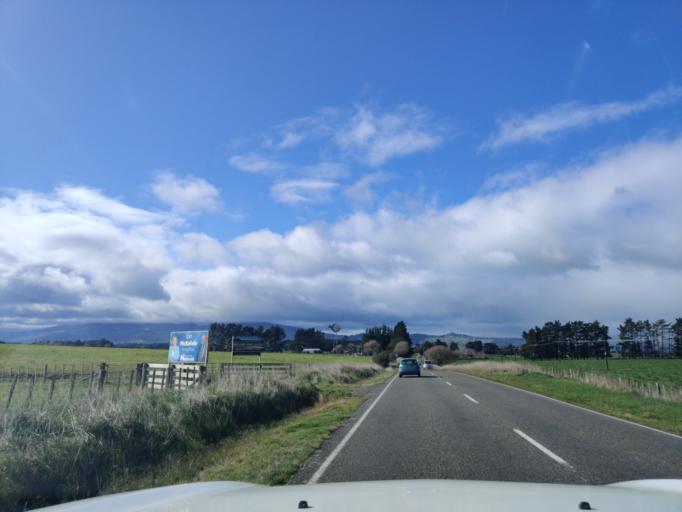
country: NZ
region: Manawatu-Wanganui
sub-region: Palmerston North City
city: Palmerston North
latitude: -40.2886
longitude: 175.6925
